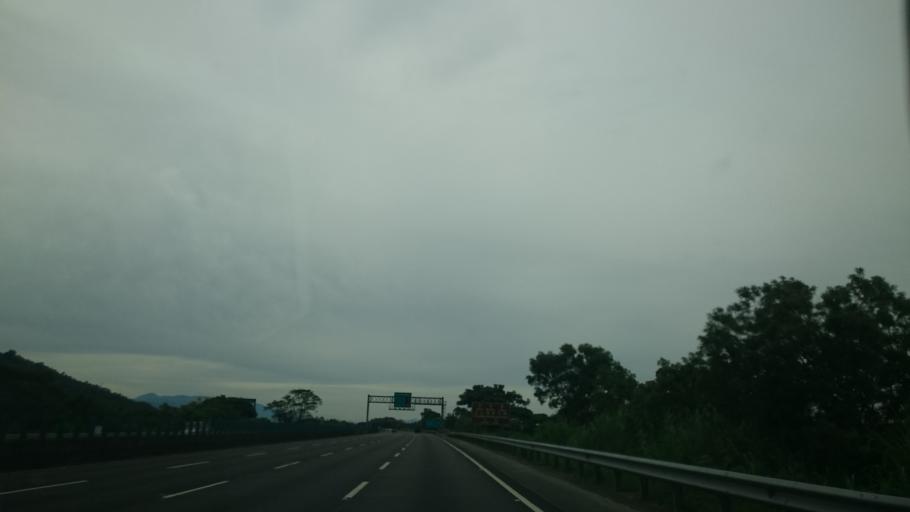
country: TW
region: Taiwan
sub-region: Nantou
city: Nantou
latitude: 23.8647
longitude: 120.7031
